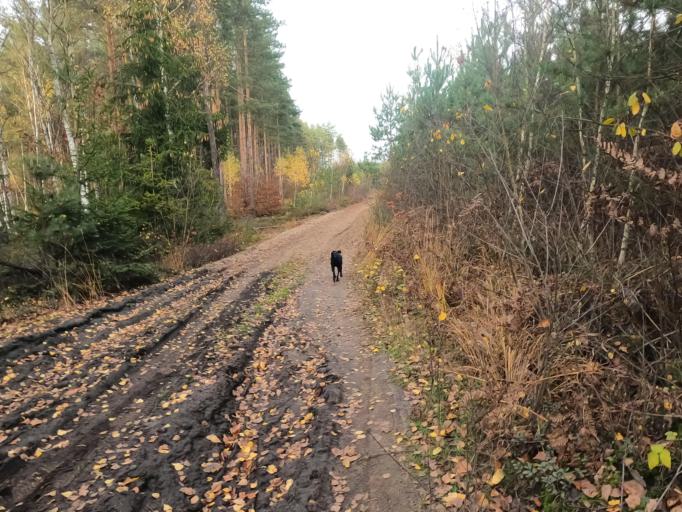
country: PL
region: Pomeranian Voivodeship
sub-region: Powiat starogardzki
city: Skarszewy
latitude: 54.0121
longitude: 18.4632
